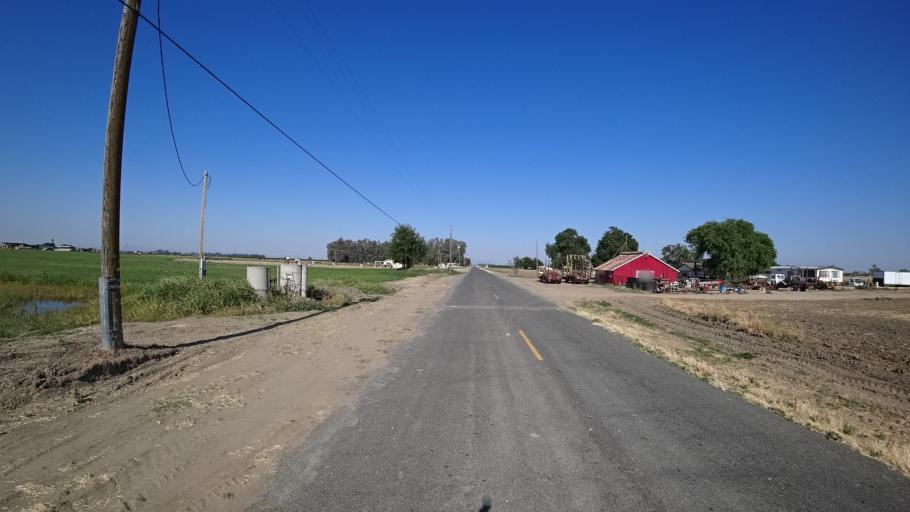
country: US
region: California
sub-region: Fresno County
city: Riverdale
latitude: 36.3657
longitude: -119.8749
